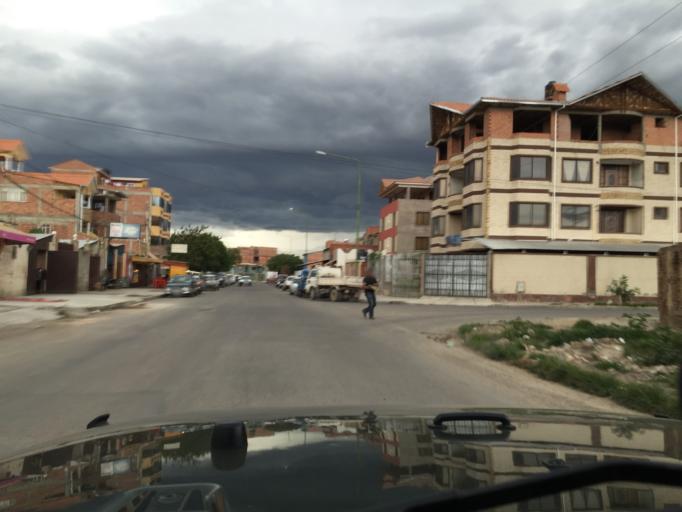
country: BO
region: Cochabamba
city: Cochabamba
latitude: -17.4167
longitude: -66.1666
